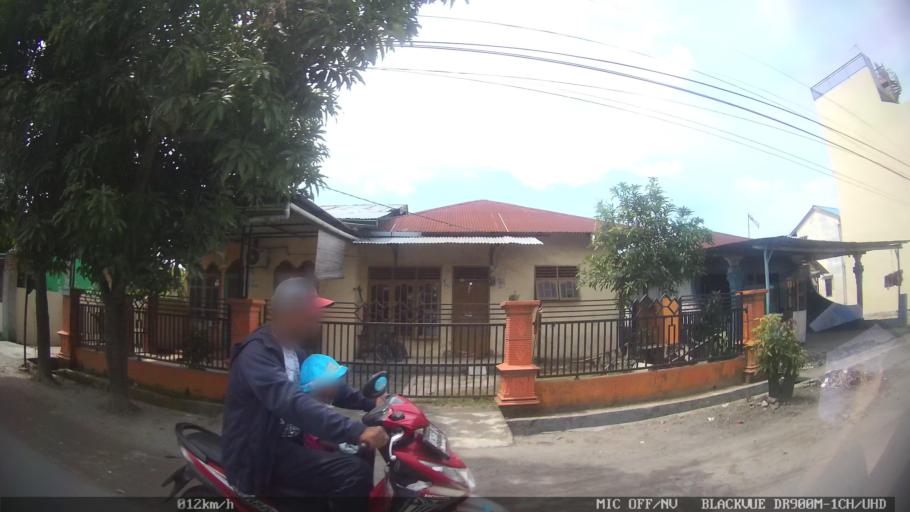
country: ID
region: North Sumatra
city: Medan
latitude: 3.6509
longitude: 98.7007
